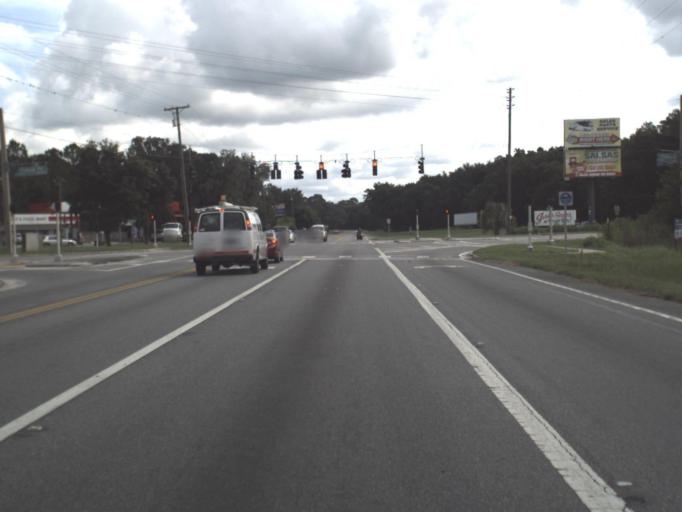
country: US
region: Florida
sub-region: Pasco County
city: Zephyrhills South
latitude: 28.2076
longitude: -82.1855
